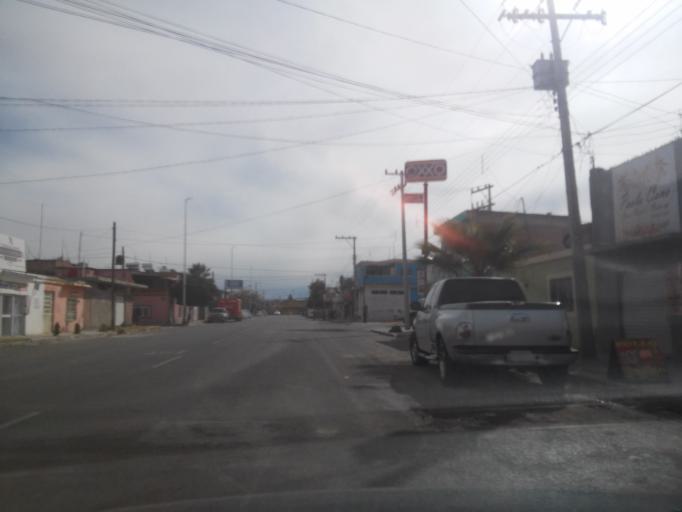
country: MX
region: Durango
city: Victoria de Durango
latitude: 24.0176
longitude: -104.6554
